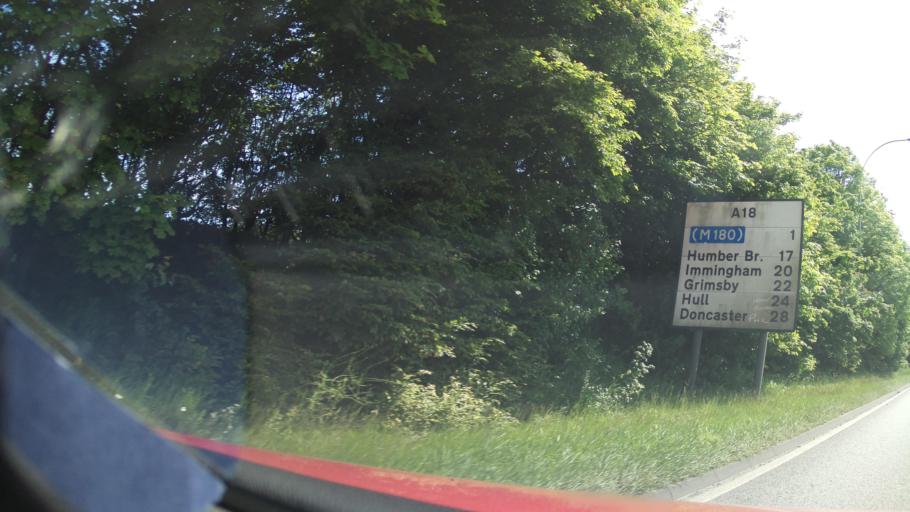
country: GB
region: England
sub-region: North Lincolnshire
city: Broughton
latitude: 53.5542
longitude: -0.5809
